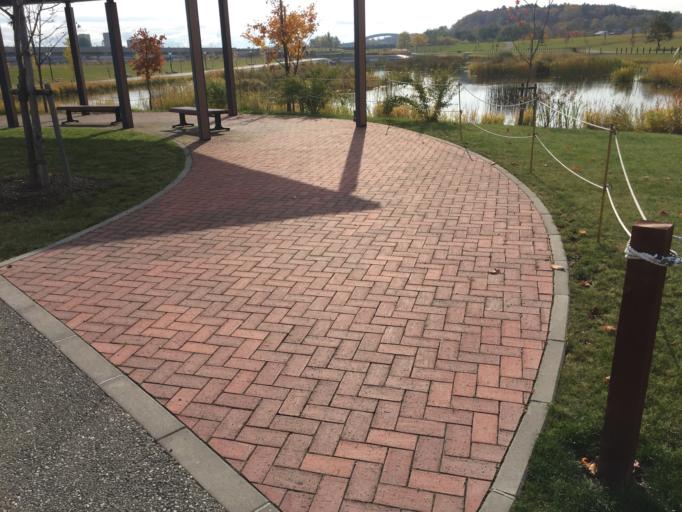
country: JP
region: Hokkaido
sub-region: Asahikawa-shi
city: Asahikawa
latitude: 43.7612
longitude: 142.3603
